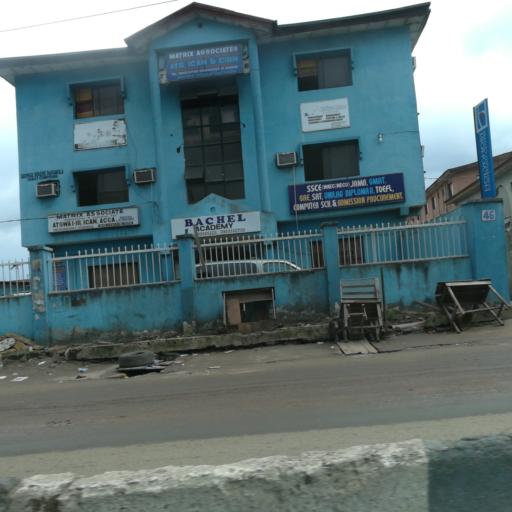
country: NG
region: Lagos
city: Agege
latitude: 6.5998
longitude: 3.2953
